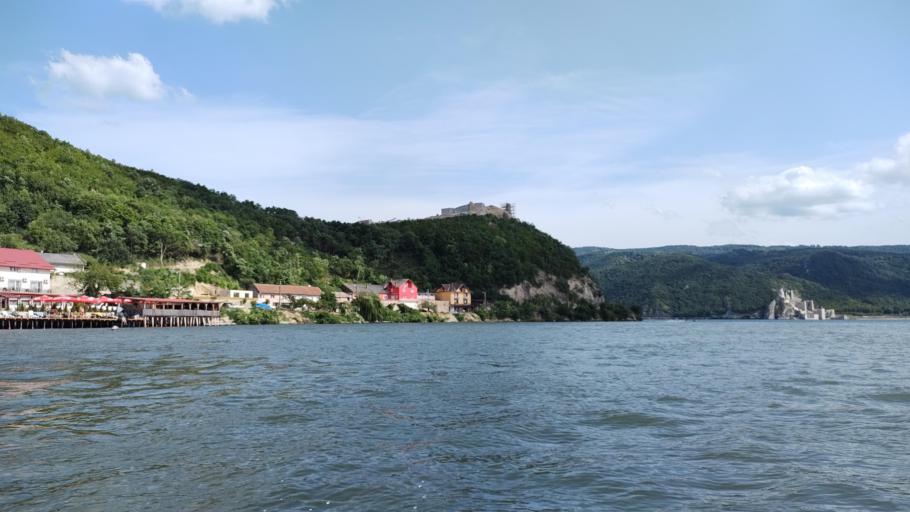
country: RO
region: Caras-Severin
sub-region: Comuna Pescari
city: Coronini
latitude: 44.6765
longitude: 21.6782
